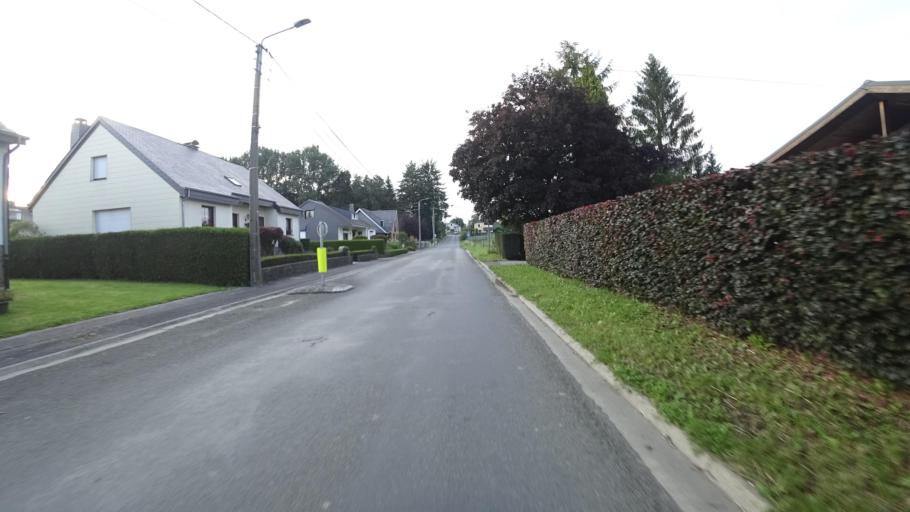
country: BE
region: Wallonia
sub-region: Province du Luxembourg
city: Neufchateau
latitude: 49.9108
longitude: 5.3842
